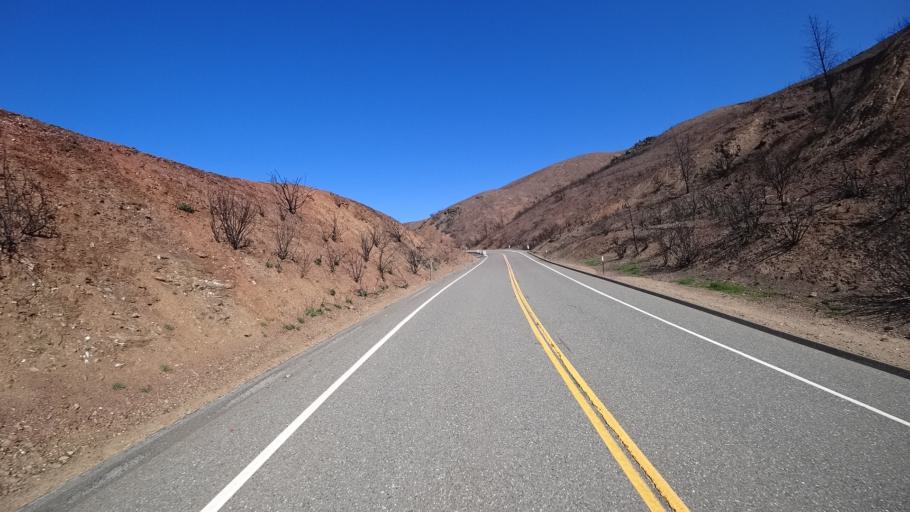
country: US
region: California
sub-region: Tehama County
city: Rancho Tehama Reserve
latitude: 39.6506
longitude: -122.6177
